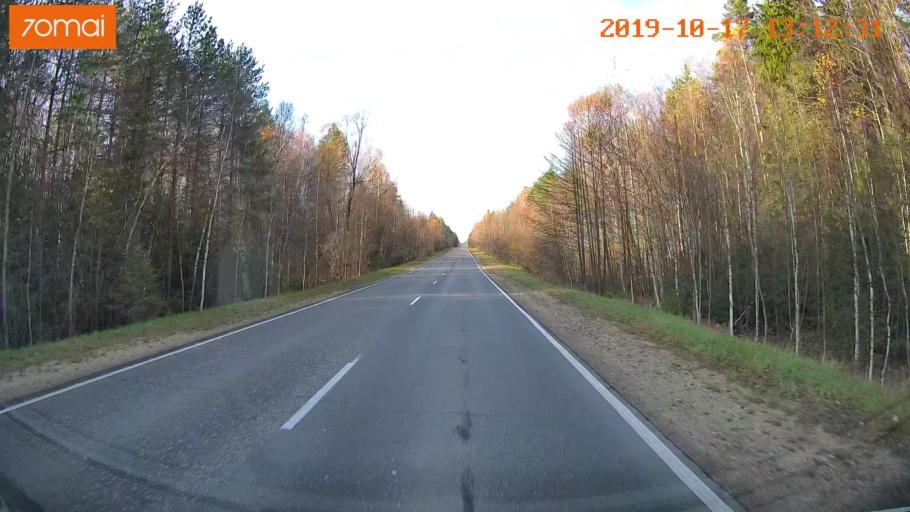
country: RU
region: Rjazan
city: Gus'-Zheleznyy
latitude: 55.0371
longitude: 41.2112
